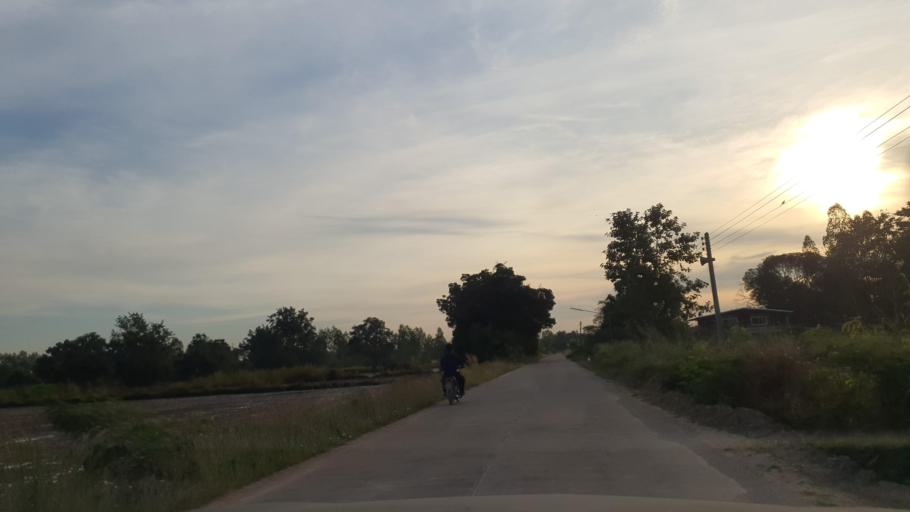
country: TH
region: Nakhon Sawan
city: Krok Phra
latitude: 15.6631
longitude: 100.0103
